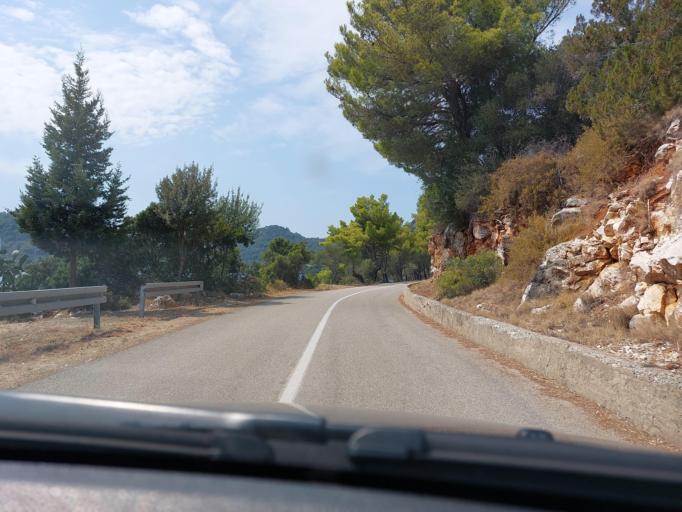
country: HR
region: Dubrovacko-Neretvanska
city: Smokvica
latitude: 42.7609
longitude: 16.8245
